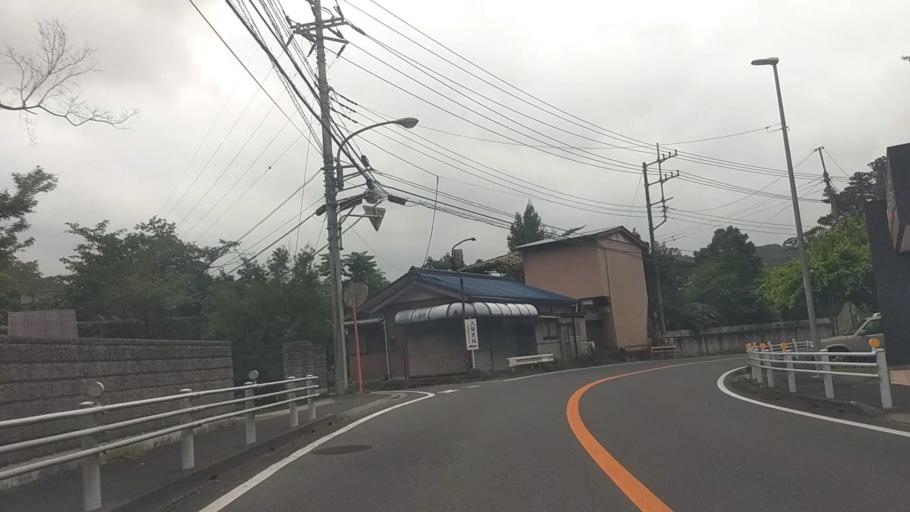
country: JP
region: Chiba
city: Kisarazu
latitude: 35.2908
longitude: 140.0837
